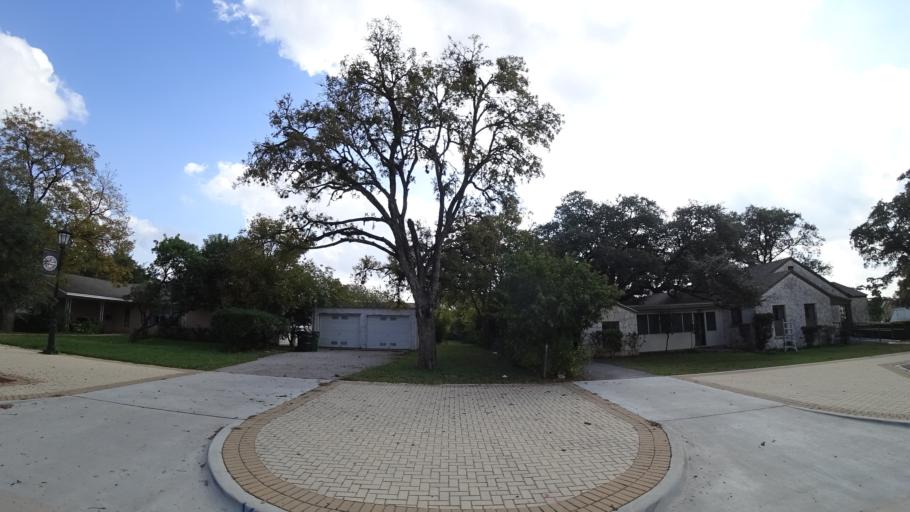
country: US
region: Texas
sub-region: Williamson County
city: Round Rock
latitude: 30.5085
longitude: -97.6829
